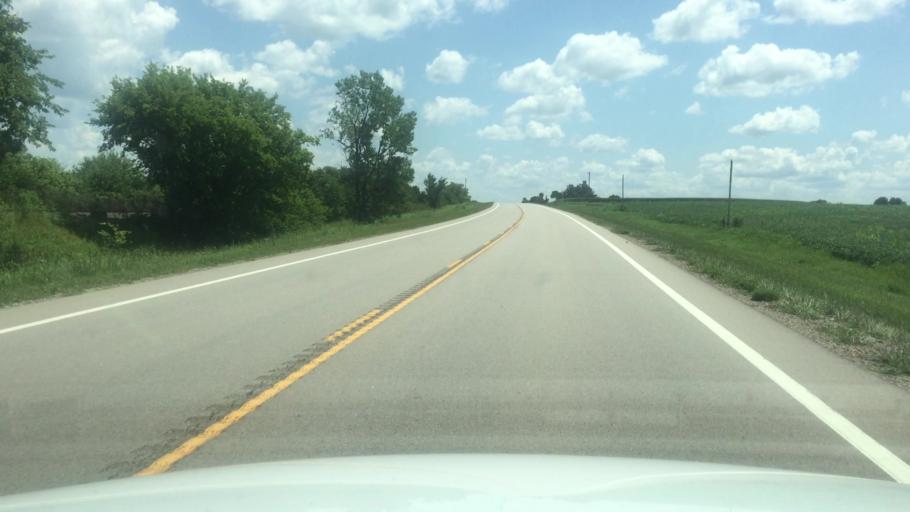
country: US
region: Kansas
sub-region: Brown County
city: Horton
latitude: 39.6118
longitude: -95.3457
